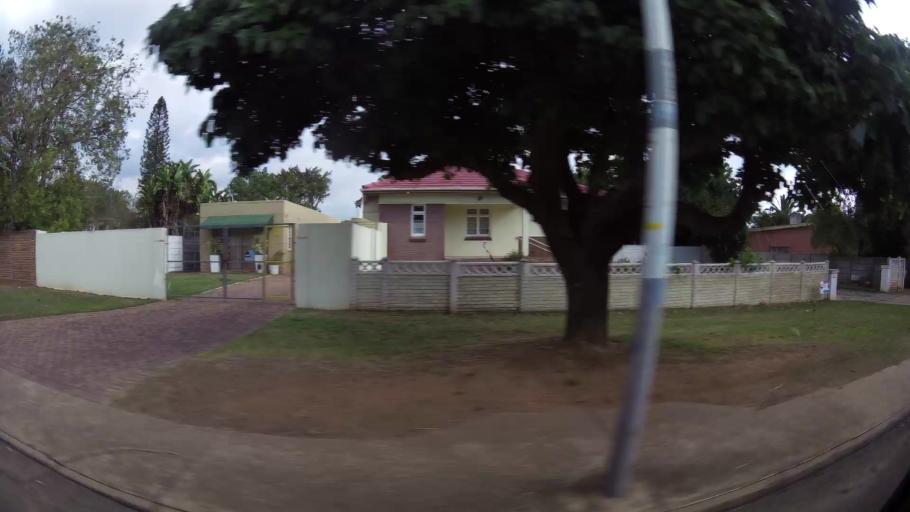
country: ZA
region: Eastern Cape
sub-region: Nelson Mandela Bay Metropolitan Municipality
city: Uitenhage
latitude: -33.7488
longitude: 25.4049
